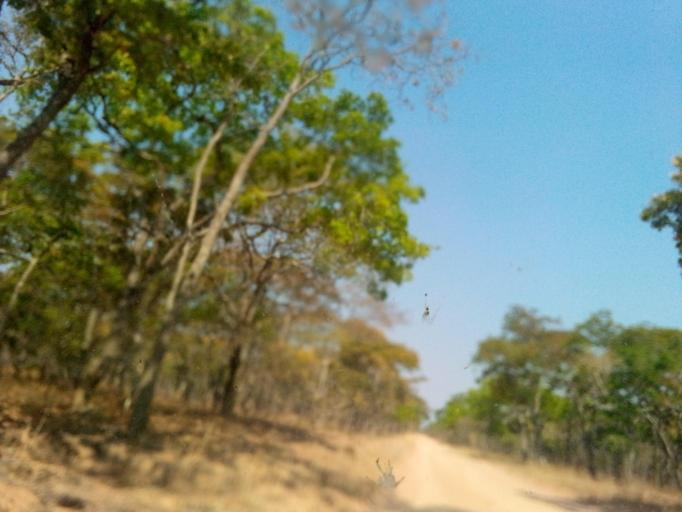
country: ZM
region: Northern
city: Mpika
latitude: -12.2419
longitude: 30.8564
